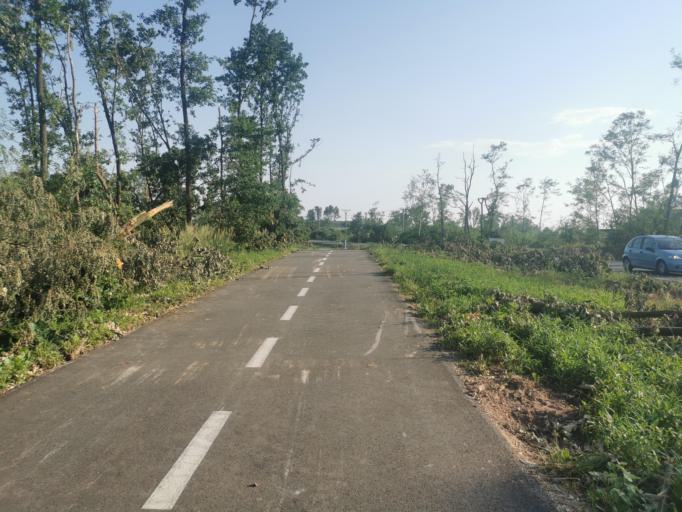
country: CZ
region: South Moravian
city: Rohatec
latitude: 48.8855
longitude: 17.1478
